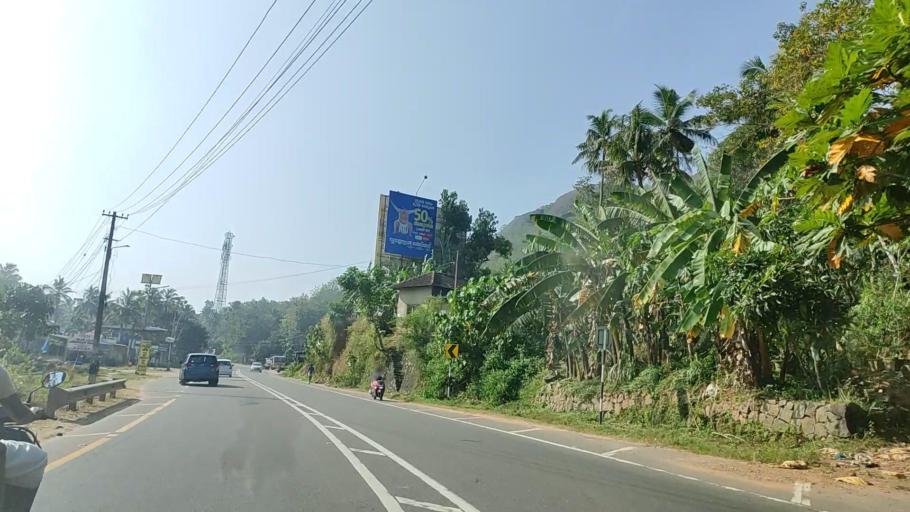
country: IN
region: Kerala
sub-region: Kollam
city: Punalur
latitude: 8.8686
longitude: 76.8701
